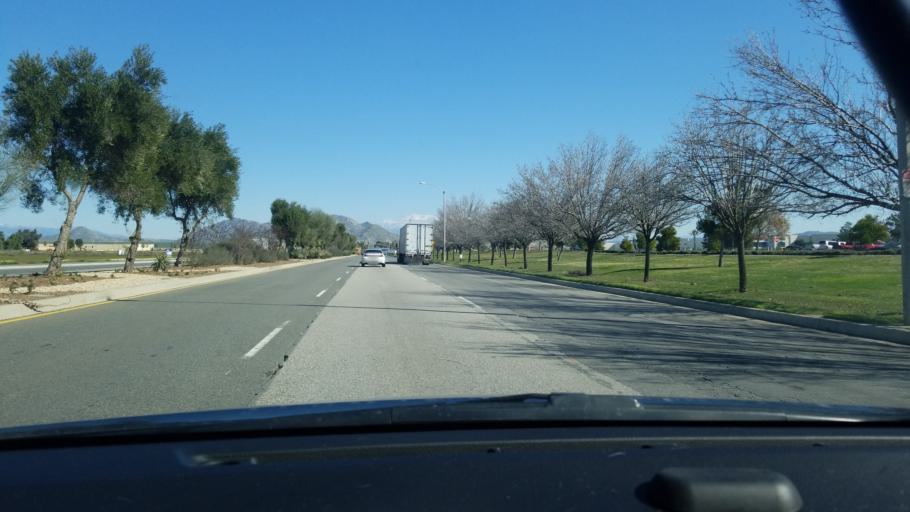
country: US
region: California
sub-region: Riverside County
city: March Air Force Base
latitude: 33.8445
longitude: -117.2347
